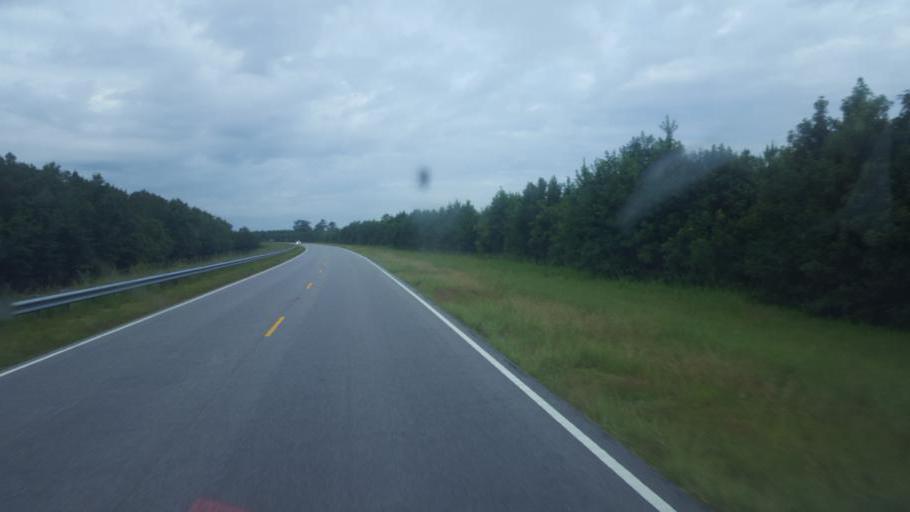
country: US
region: North Carolina
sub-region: Tyrrell County
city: Columbia
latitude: 35.9338
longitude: -76.1553
